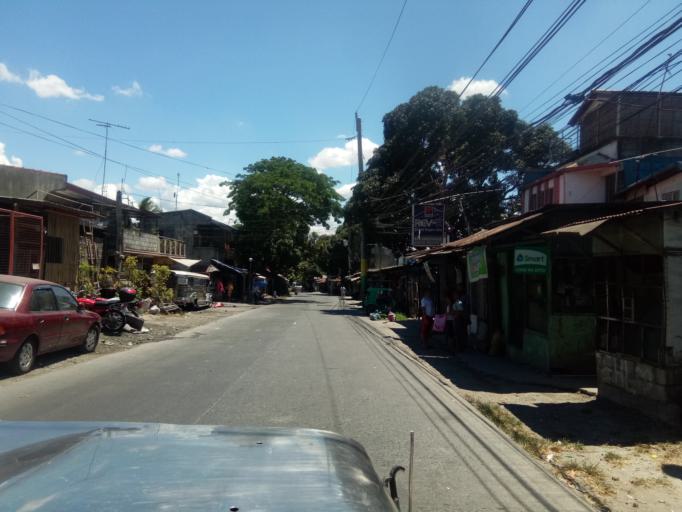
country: PH
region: Calabarzon
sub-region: Province of Cavite
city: Dasmarinas
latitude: 14.3240
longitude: 120.9672
